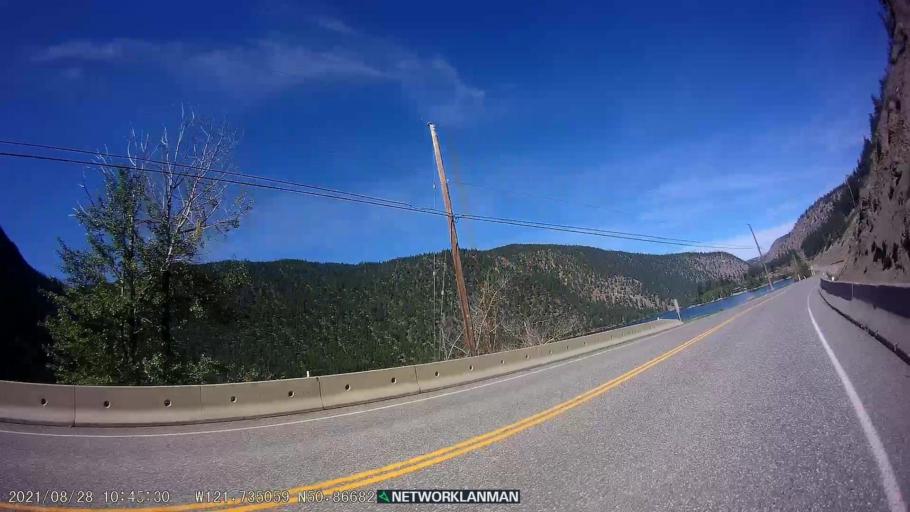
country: CA
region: British Columbia
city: Lillooet
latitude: 50.8662
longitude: -121.7354
